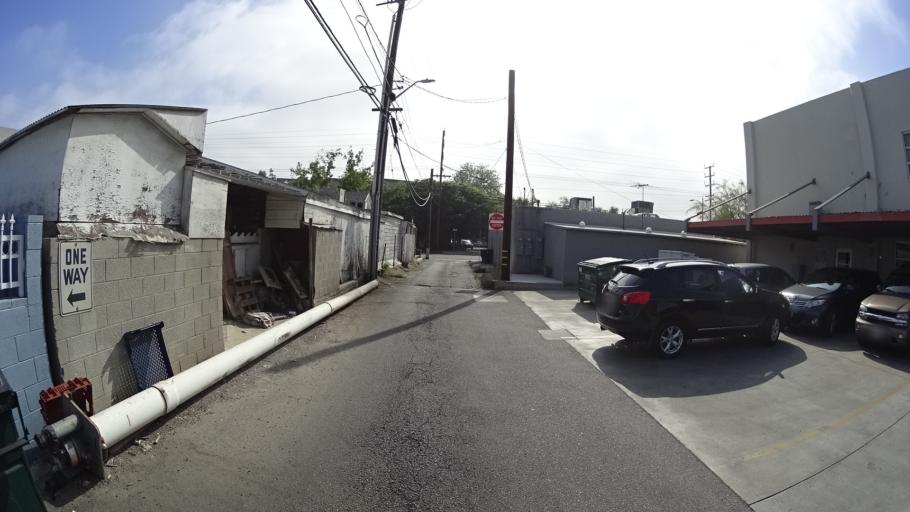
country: US
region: California
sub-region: Los Angeles County
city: Burbank
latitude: 34.1644
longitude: -118.3128
